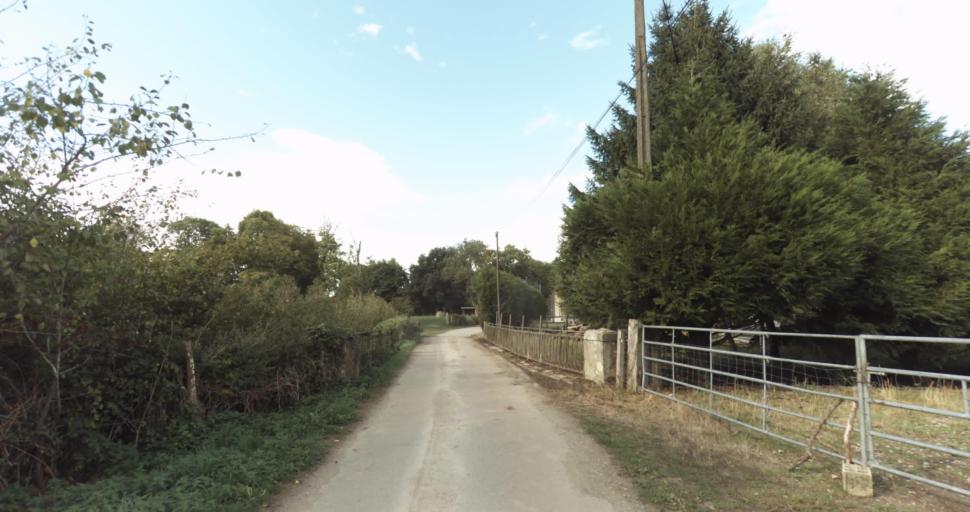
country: FR
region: Lower Normandy
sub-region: Departement de l'Orne
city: Sainte-Gauburge-Sainte-Colombe
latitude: 48.7568
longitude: 0.4020
